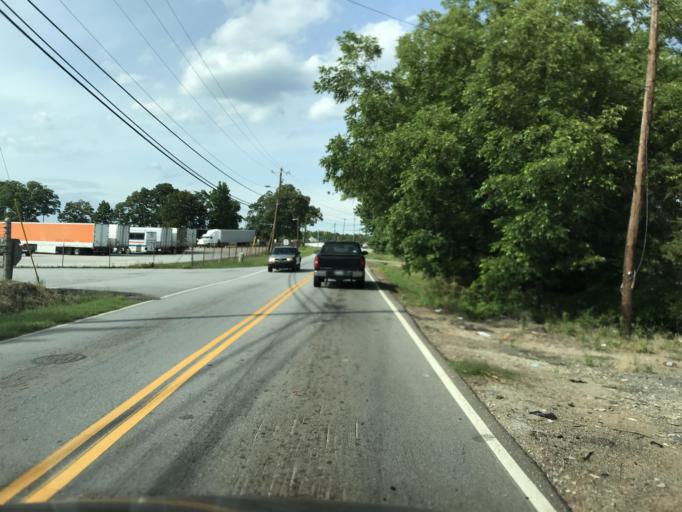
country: US
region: South Carolina
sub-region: Greenville County
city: Gantt
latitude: 34.7836
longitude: -82.4122
